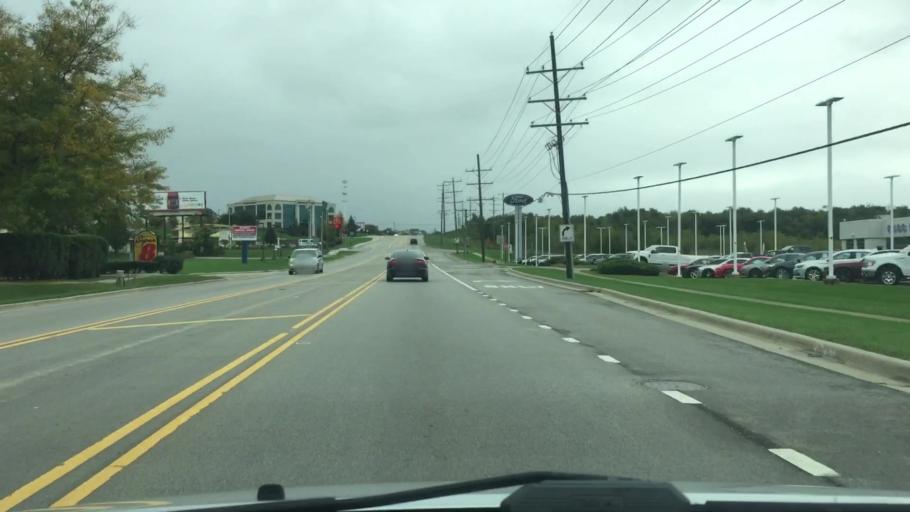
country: US
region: Illinois
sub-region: McHenry County
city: McHenry
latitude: 42.3280
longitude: -88.2744
